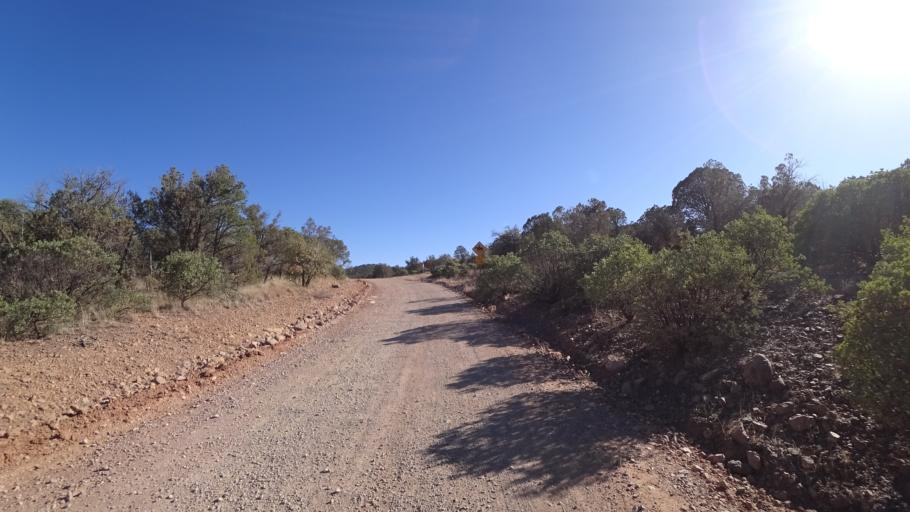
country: US
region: Arizona
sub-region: Cochise County
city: Huachuca City
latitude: 31.5132
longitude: -110.5571
